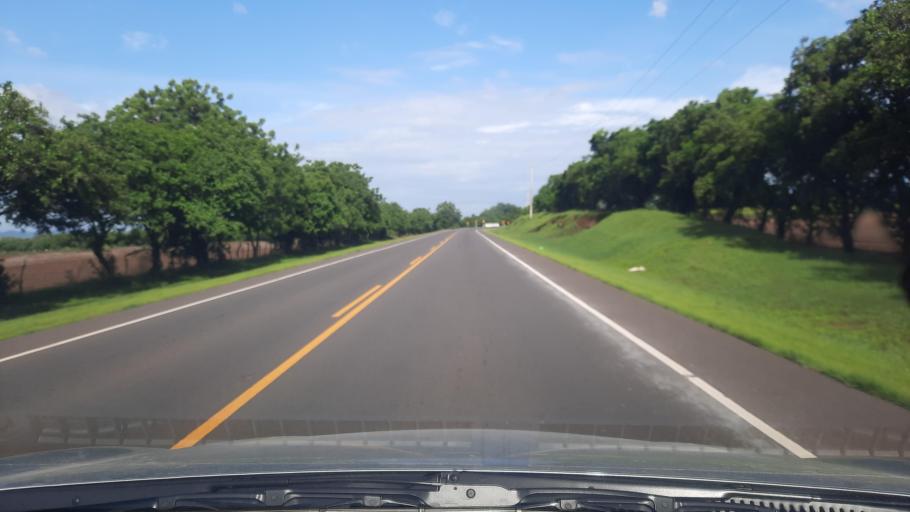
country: NI
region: Chinandega
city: Chichigalpa
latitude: 12.7640
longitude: -86.9022
